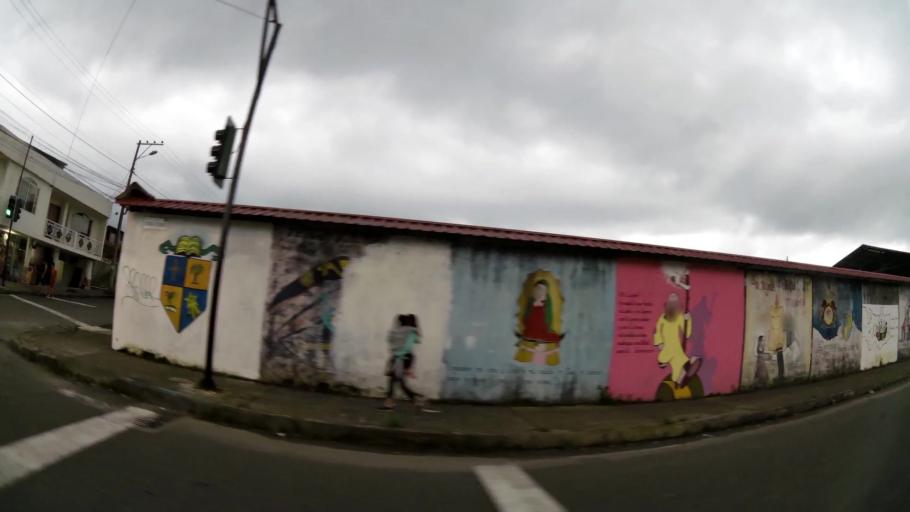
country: EC
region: Pastaza
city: Puyo
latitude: -1.4834
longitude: -78.0053
